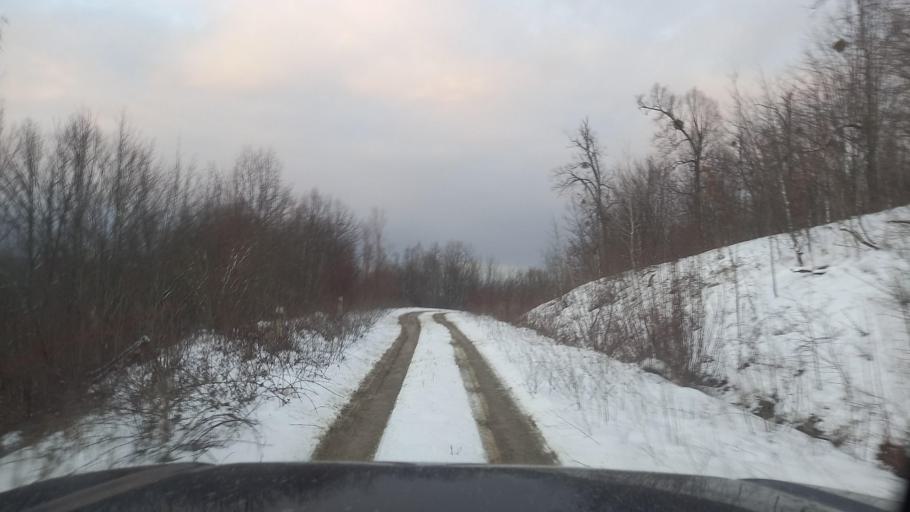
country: RU
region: Krasnodarskiy
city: Smolenskaya
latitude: 44.6720
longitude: 38.7942
